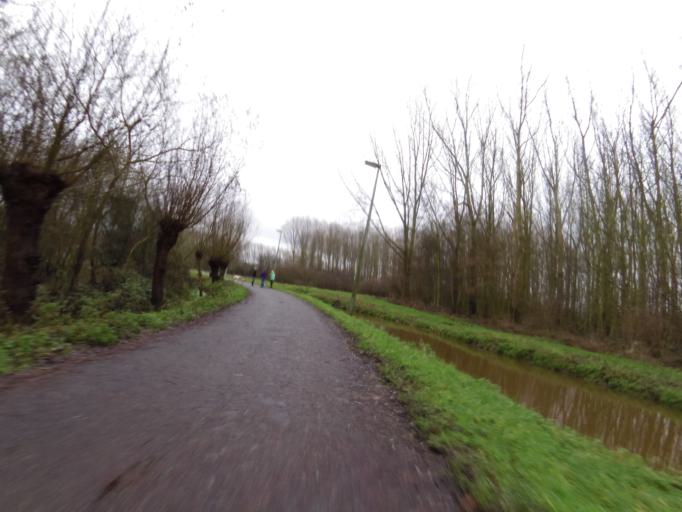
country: NL
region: South Holland
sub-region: Gemeente Vlaardingen
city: Vlaardingen
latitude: 51.9077
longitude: 4.3019
